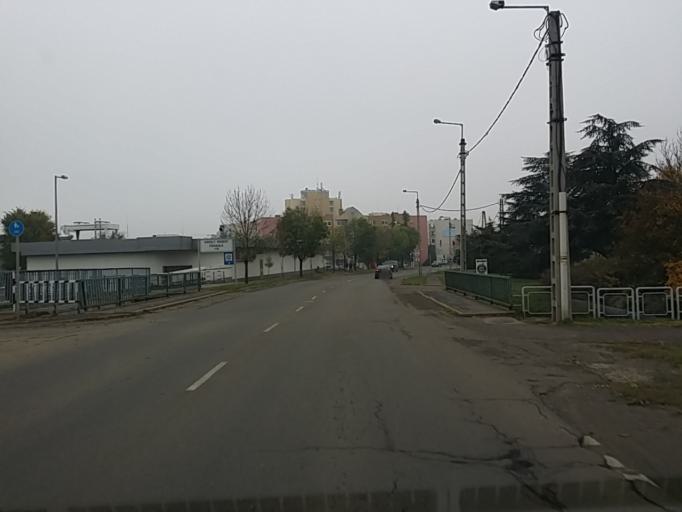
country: HU
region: Heves
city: Gyongyos
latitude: 47.7901
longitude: 19.9373
